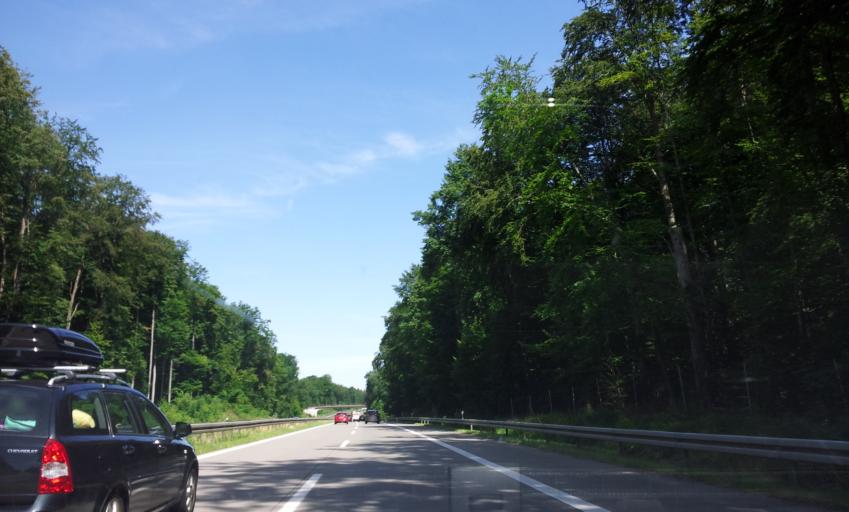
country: DE
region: Brandenburg
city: Althuttendorf
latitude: 52.9963
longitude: 13.8225
